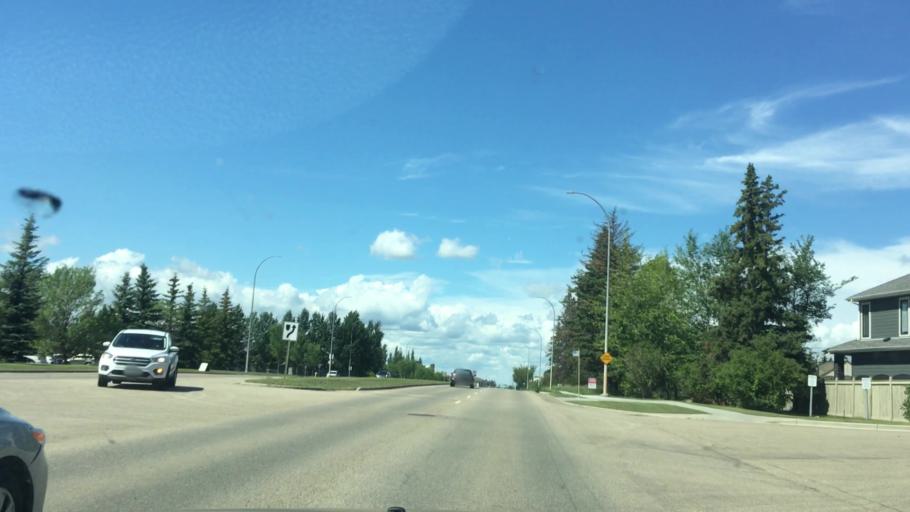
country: CA
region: Alberta
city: Beaumont
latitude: 53.4250
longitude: -113.5013
